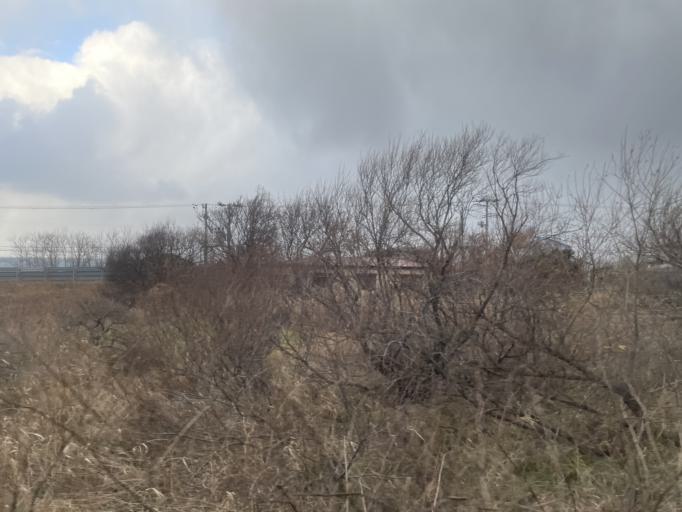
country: JP
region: Aomori
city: Mutsu
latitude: 41.1262
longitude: 141.2677
